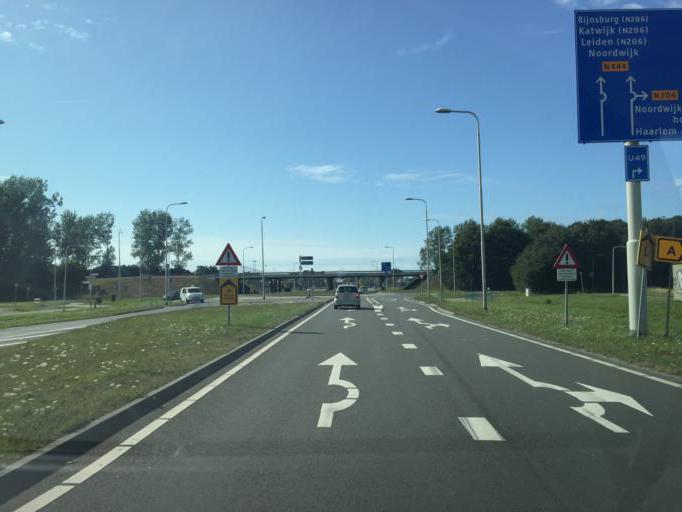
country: NL
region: South Holland
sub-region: Gemeente Noordwijk
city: Noordwijk-Binnen
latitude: 52.2299
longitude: 4.4652
